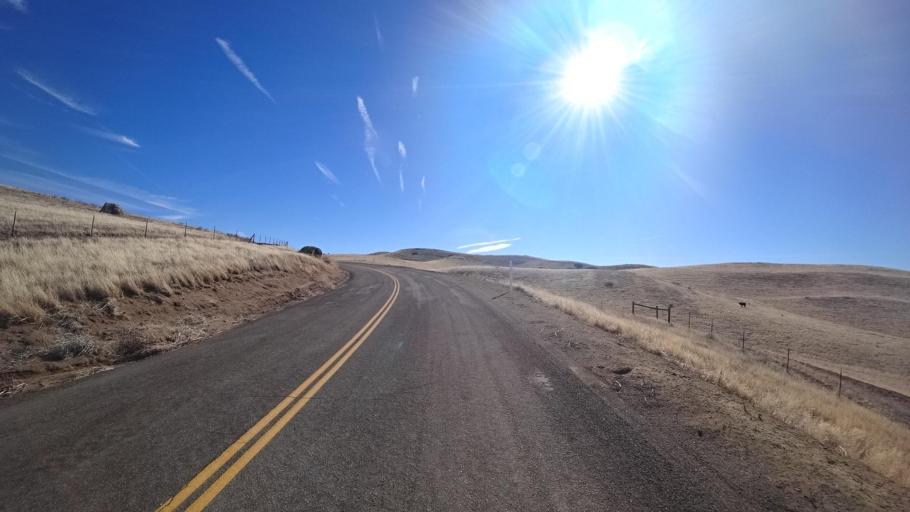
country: US
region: California
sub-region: Kern County
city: Maricopa
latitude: 34.9080
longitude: -119.3931
